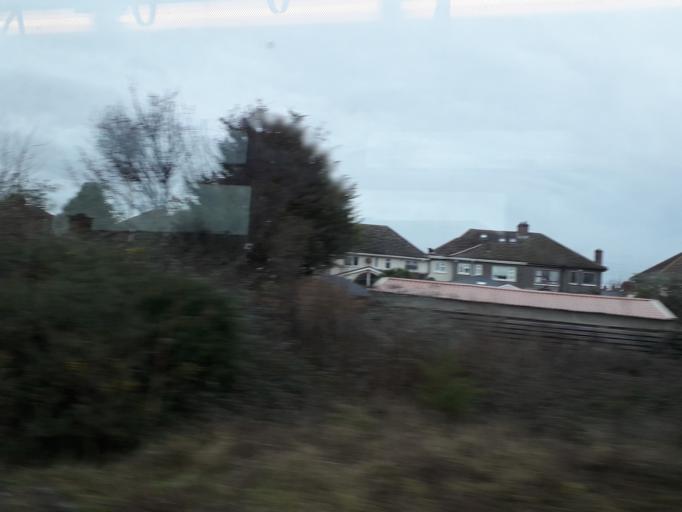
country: IE
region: Leinster
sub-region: Fingal County
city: Baldoyle
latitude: 53.3918
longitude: -6.1229
